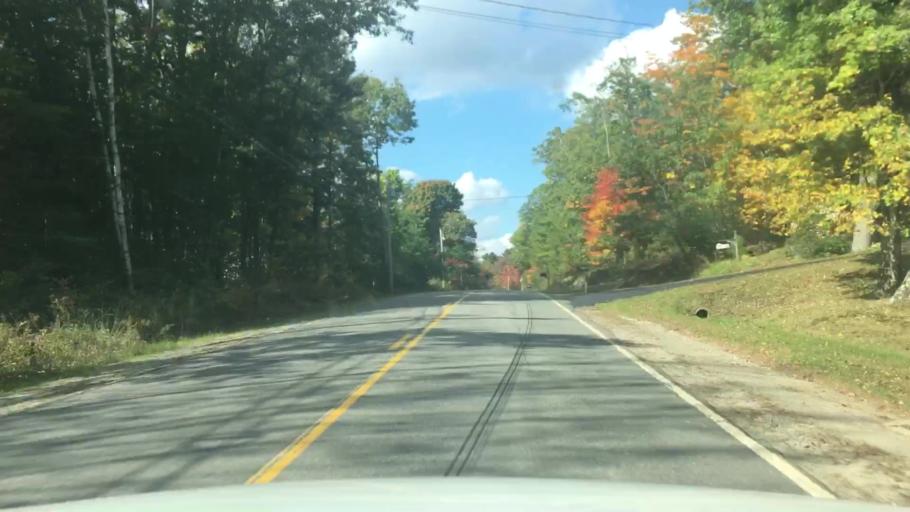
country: US
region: Maine
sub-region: Knox County
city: Warren
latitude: 44.1657
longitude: -69.2471
